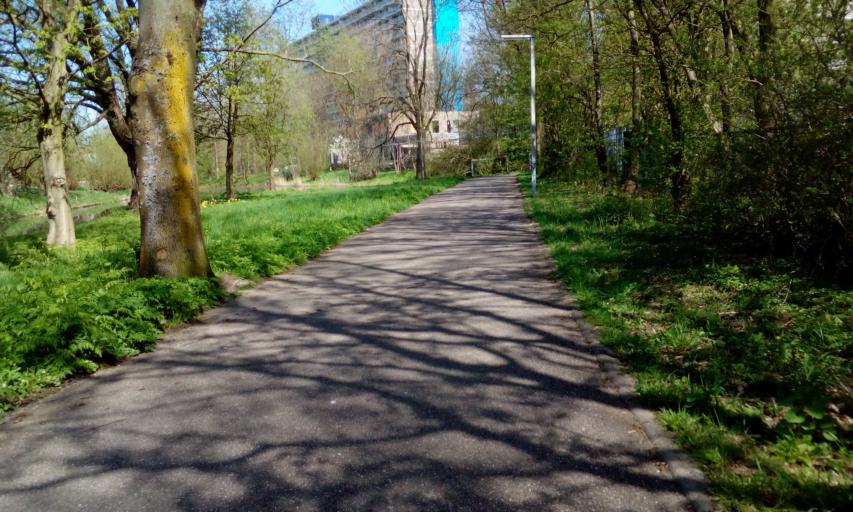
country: NL
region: South Holland
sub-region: Gemeente Delft
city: Delft
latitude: 51.9925
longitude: 4.3335
